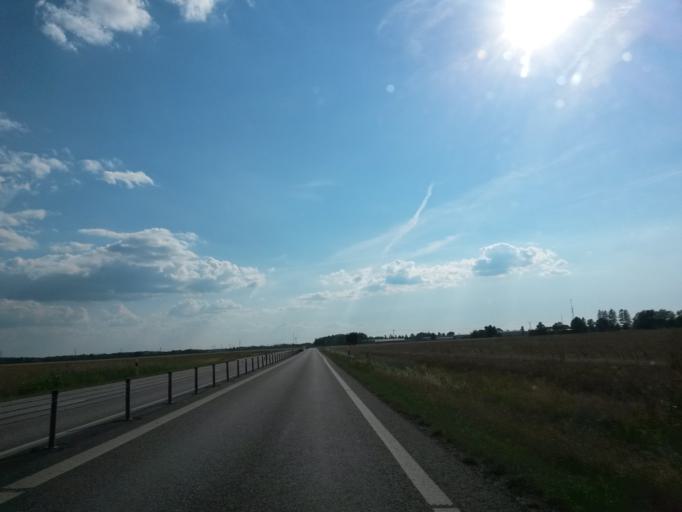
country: SE
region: Vaestra Goetaland
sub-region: Vara Kommun
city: Vara
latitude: 58.2658
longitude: 12.9953
